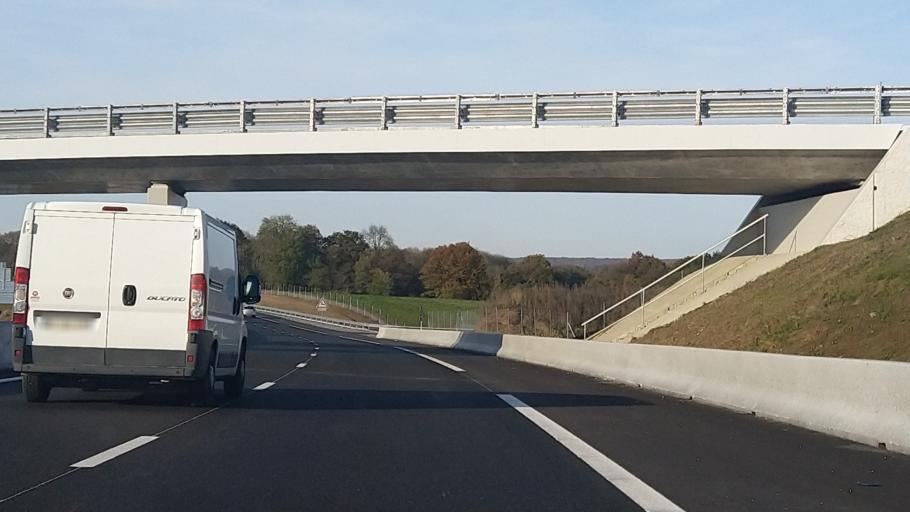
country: FR
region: Ile-de-France
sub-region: Departement du Val-d'Oise
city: Montsoult
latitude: 49.0771
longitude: 2.3324
